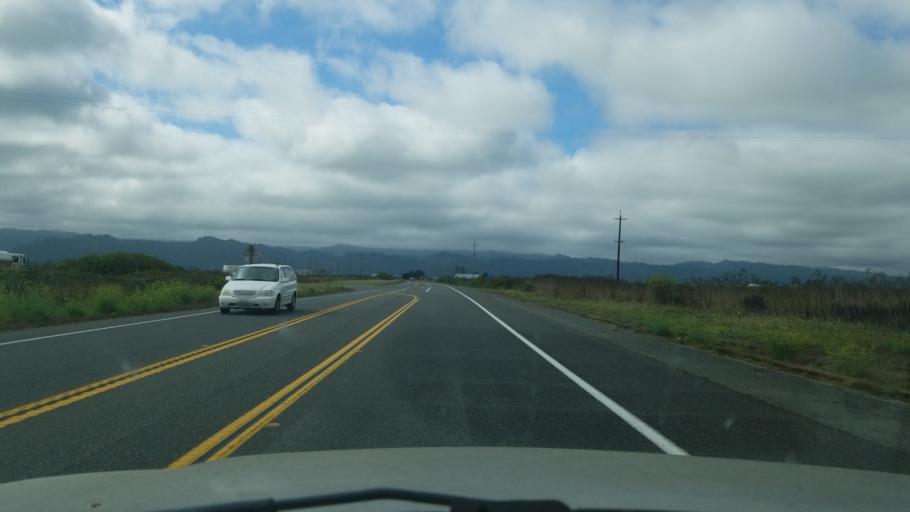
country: US
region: California
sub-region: Humboldt County
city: Fortuna
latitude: 40.6070
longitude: -124.2075
